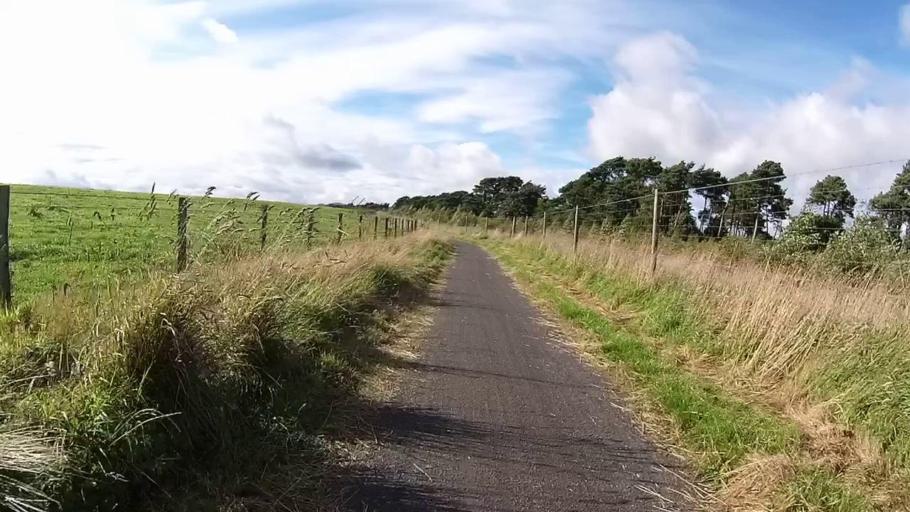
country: GB
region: Scotland
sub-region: Perth and Kinross
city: Kinross
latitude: 56.1890
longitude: -3.3979
